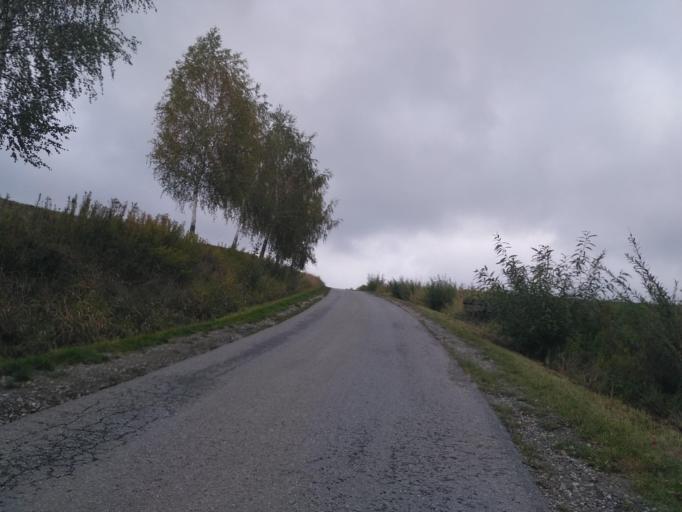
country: PL
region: Subcarpathian Voivodeship
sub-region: Powiat debicki
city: Brzostek
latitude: 49.9224
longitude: 21.4459
